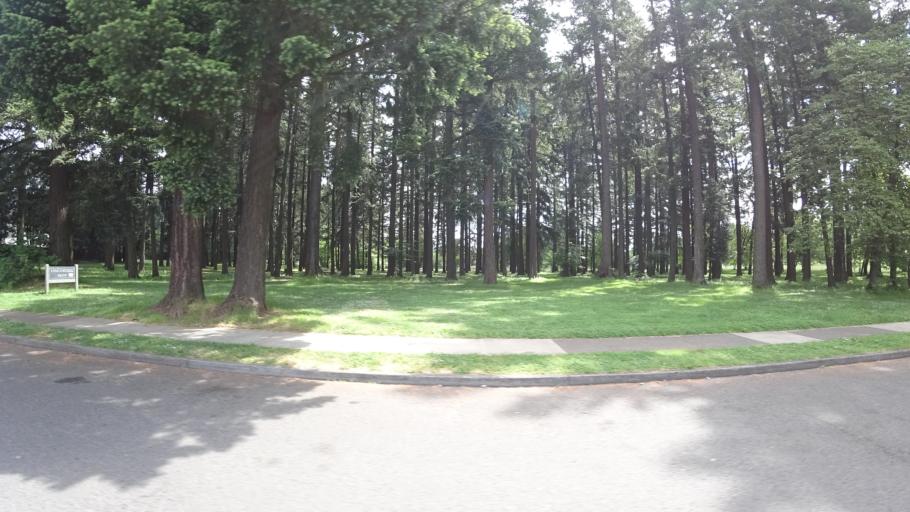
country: US
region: Oregon
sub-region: Multnomah County
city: Gresham
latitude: 45.4984
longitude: -122.4879
